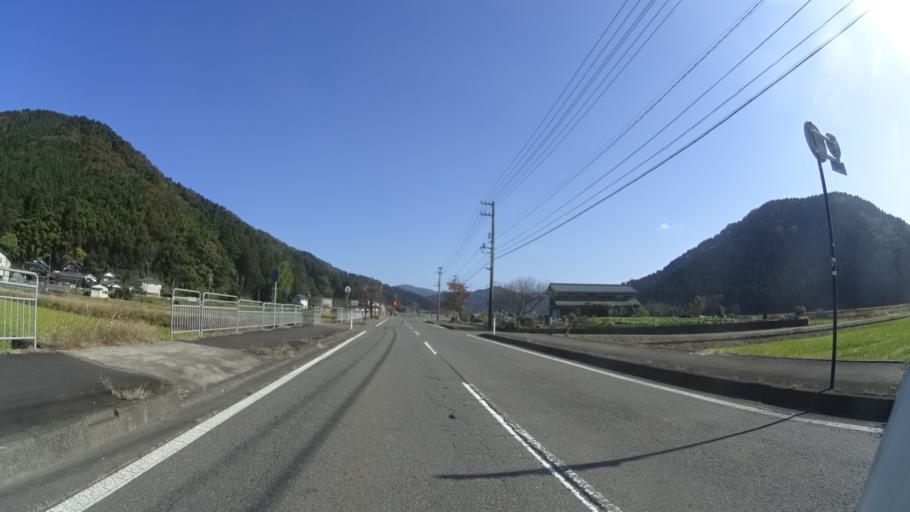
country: JP
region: Fukui
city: Sabae
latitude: 35.9488
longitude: 136.2486
